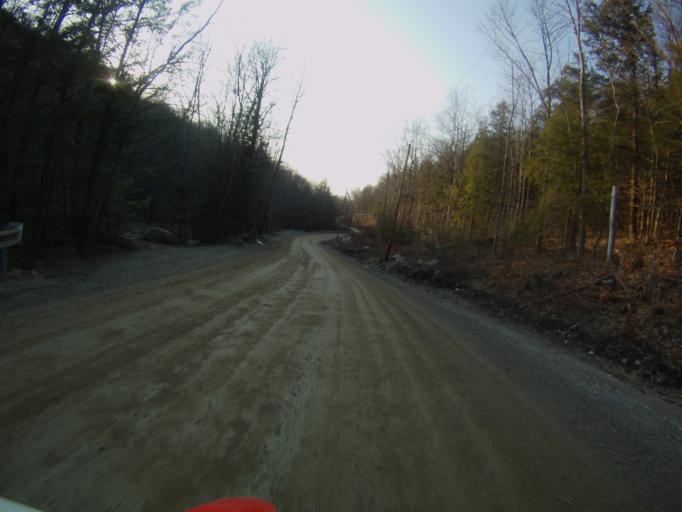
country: US
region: Vermont
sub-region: Addison County
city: Bristol
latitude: 44.0764
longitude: -73.0614
